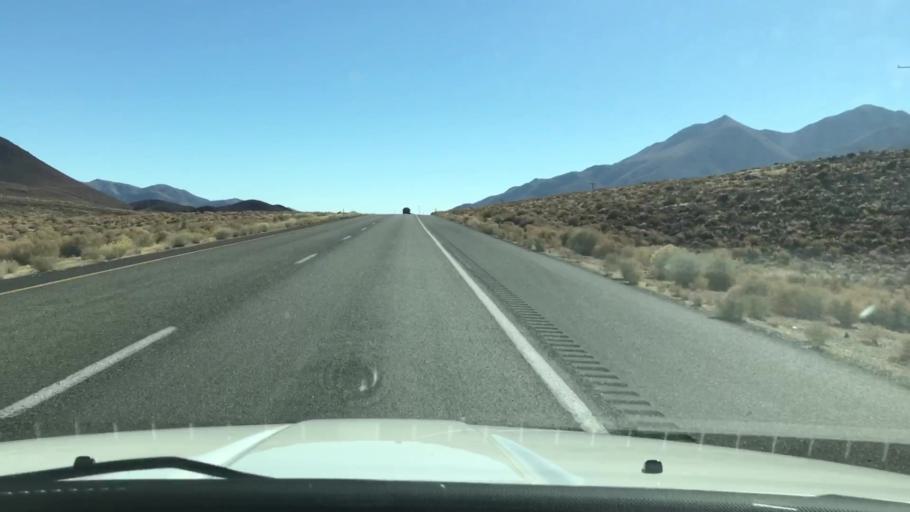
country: US
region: California
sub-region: Kern County
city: Inyokern
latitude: 36.0009
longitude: -117.9338
